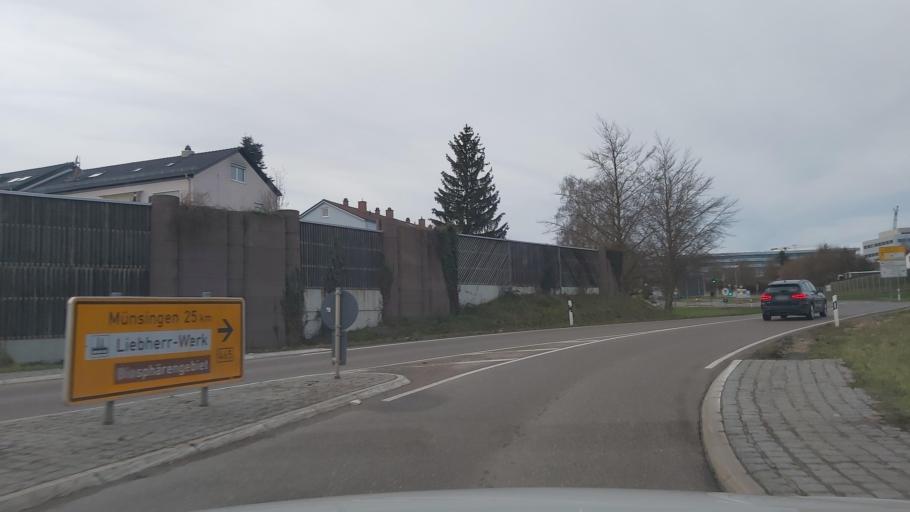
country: DE
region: Baden-Wuerttemberg
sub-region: Tuebingen Region
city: Ehingen
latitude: 48.2899
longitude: 9.7156
